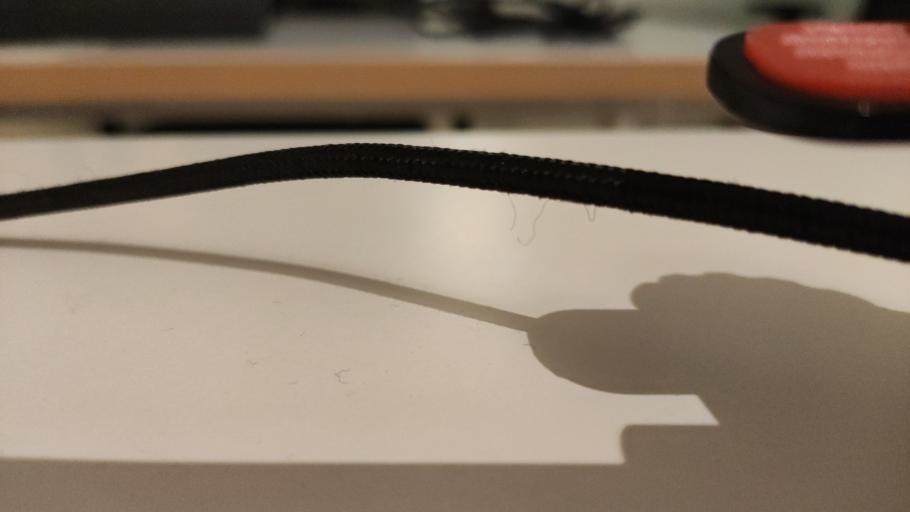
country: RU
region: Moskovskaya
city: Orekhovo-Zuyevo
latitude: 55.8328
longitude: 38.9669
